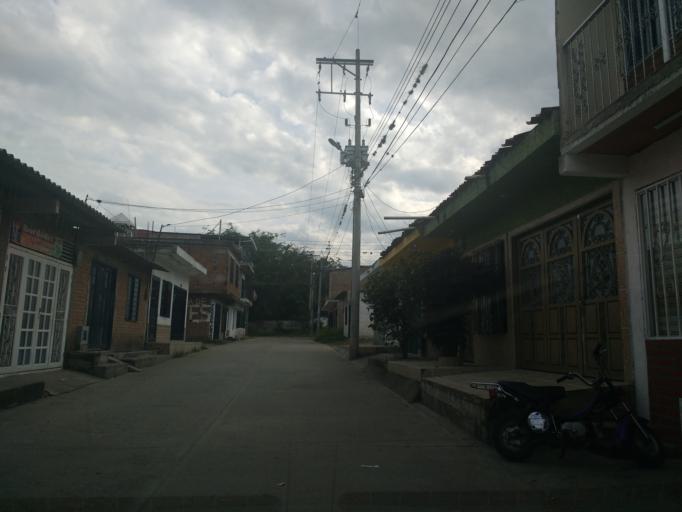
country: CO
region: Cauca
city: Miranda
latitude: 3.2559
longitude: -76.2301
